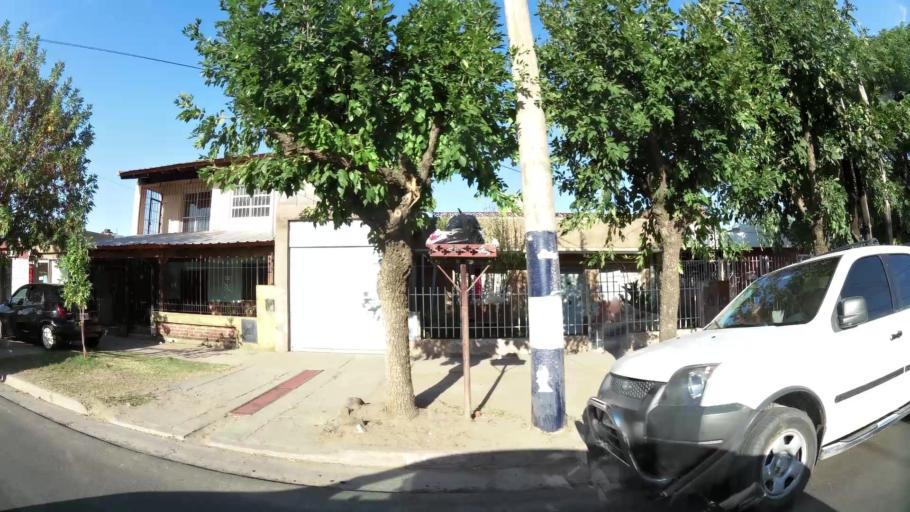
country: AR
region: Cordoba
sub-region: Departamento de Capital
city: Cordoba
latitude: -31.4461
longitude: -64.2481
